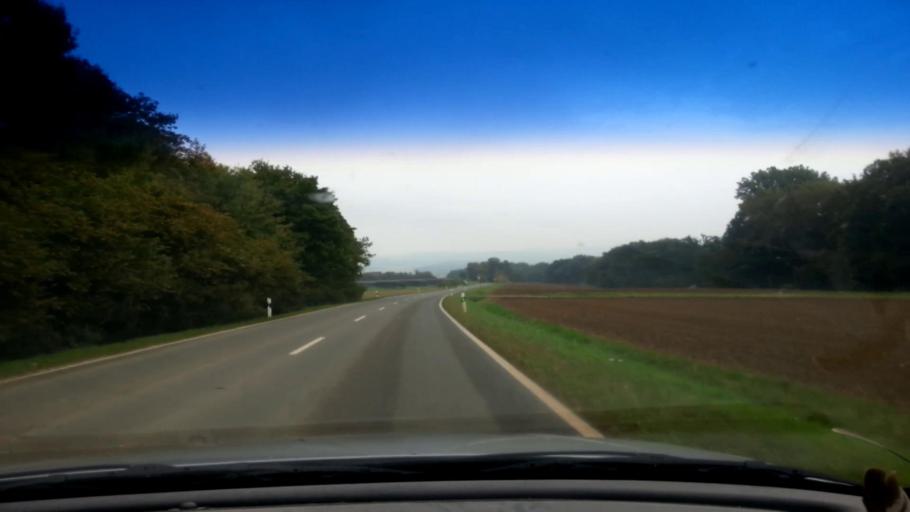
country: DE
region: Bavaria
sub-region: Upper Franconia
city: Ebensfeld
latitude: 50.0657
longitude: 10.9283
